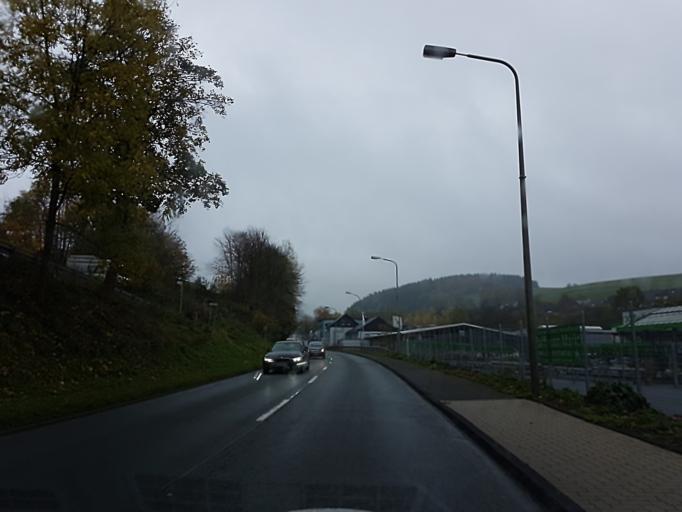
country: DE
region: North Rhine-Westphalia
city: Kierspe
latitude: 51.1285
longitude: 7.6196
